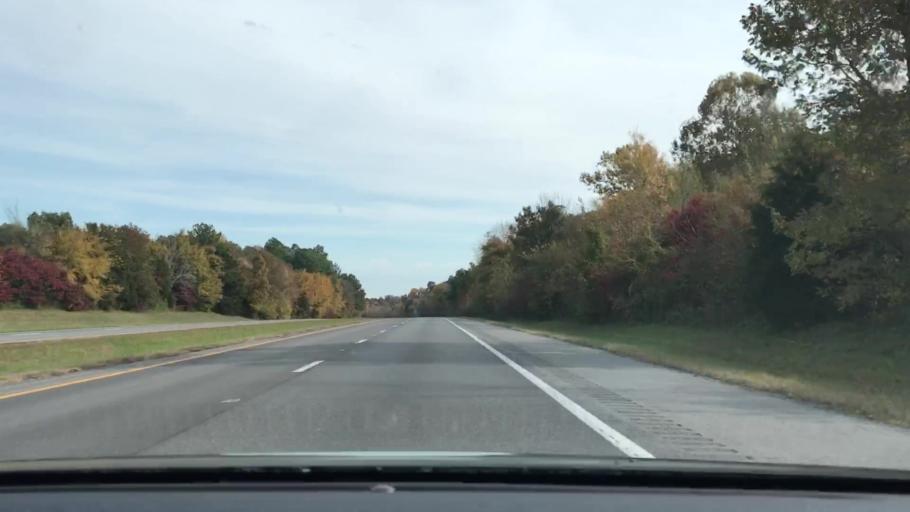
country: US
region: Kentucky
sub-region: Marshall County
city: Benton
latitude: 36.8382
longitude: -88.4242
